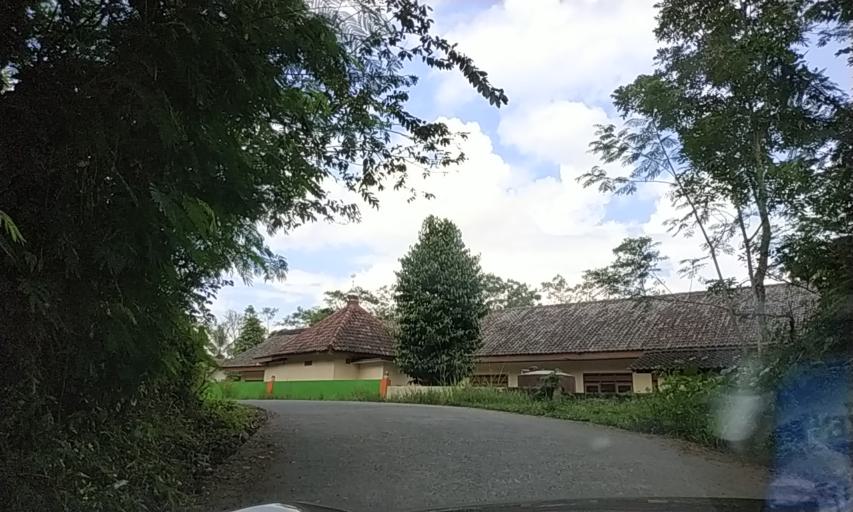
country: ID
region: Central Java
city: Jogonalan
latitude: -7.6286
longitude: 110.4734
